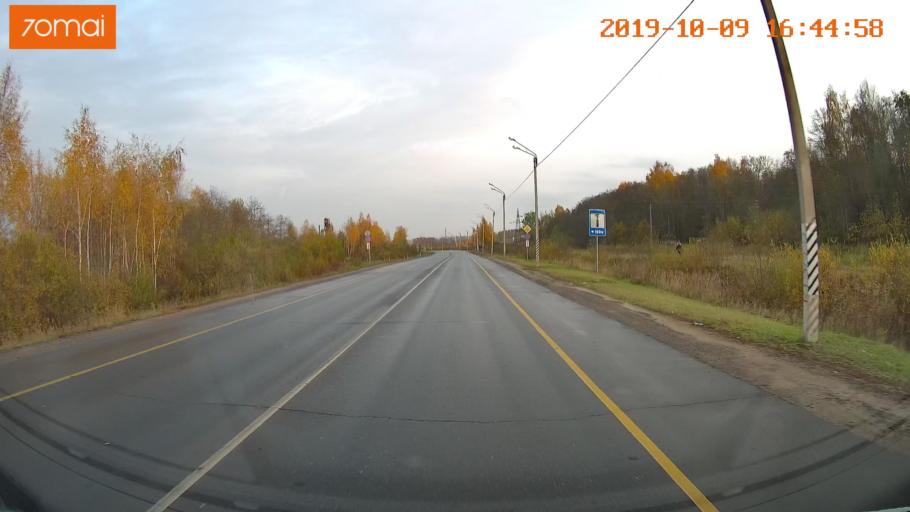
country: RU
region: Kostroma
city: Volgorechensk
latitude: 57.4491
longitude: 41.1479
